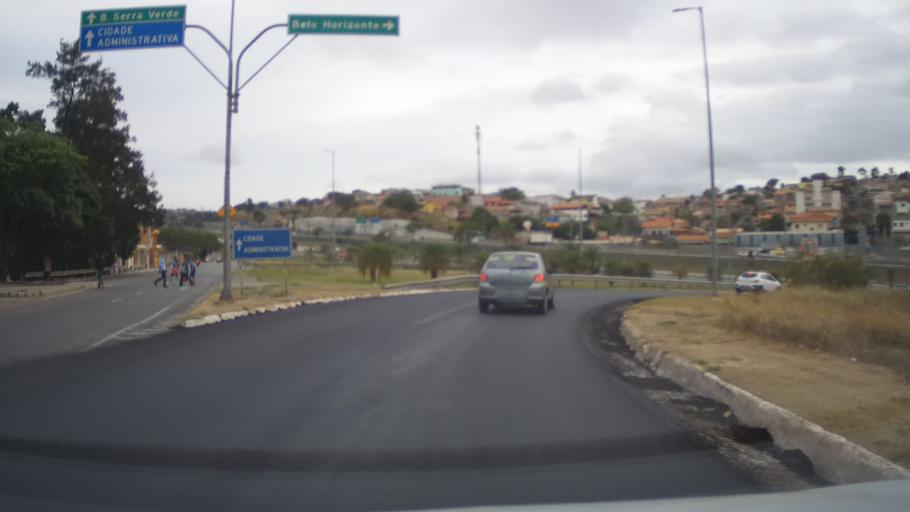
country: BR
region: Minas Gerais
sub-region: Santa Luzia
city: Santa Luzia
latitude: -19.7994
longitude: -43.9511
